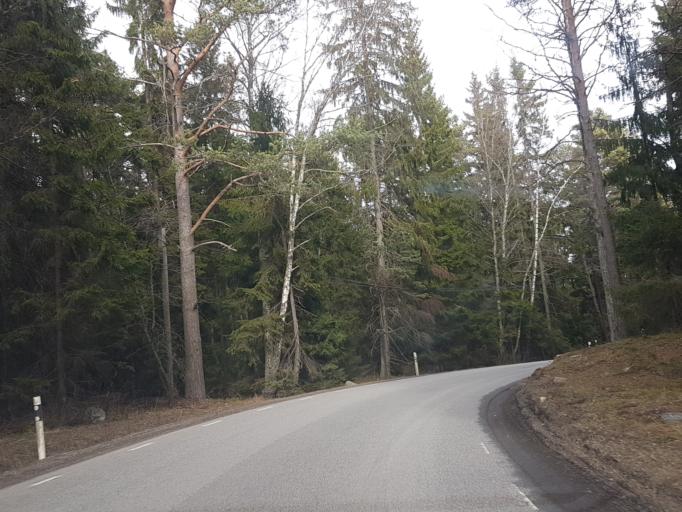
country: SE
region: Stockholm
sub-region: Norrtalje Kommun
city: Norrtalje
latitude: 59.6823
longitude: 18.8332
